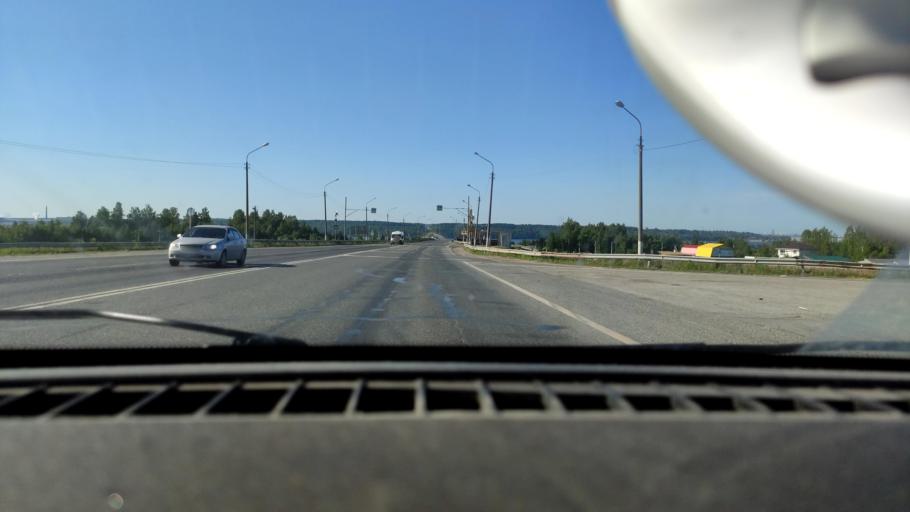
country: RU
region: Perm
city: Polazna
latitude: 58.1840
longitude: 56.4137
